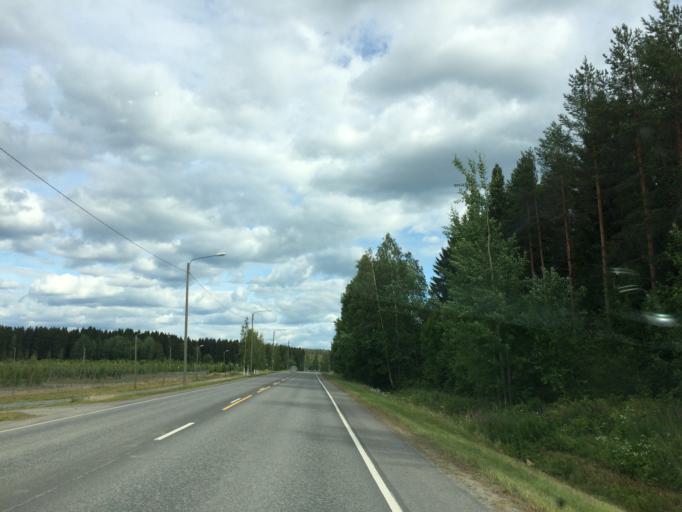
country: FI
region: Haeme
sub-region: Haemeenlinna
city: Turenki
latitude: 60.9564
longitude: 24.5969
